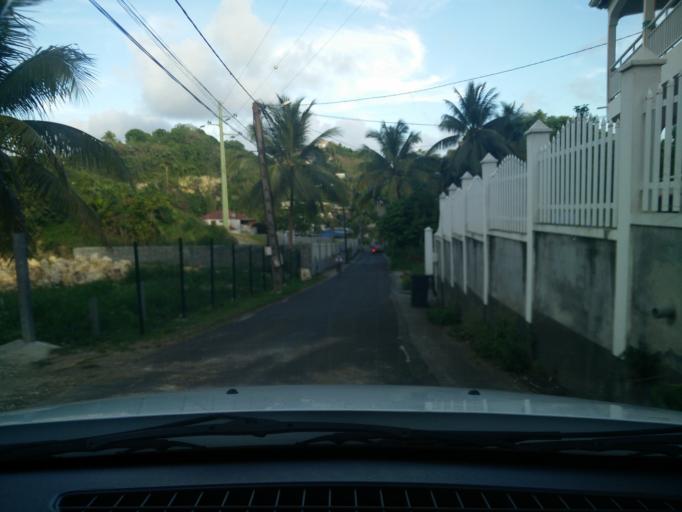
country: GP
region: Guadeloupe
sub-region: Guadeloupe
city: Les Abymes
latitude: 16.2488
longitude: -61.4943
